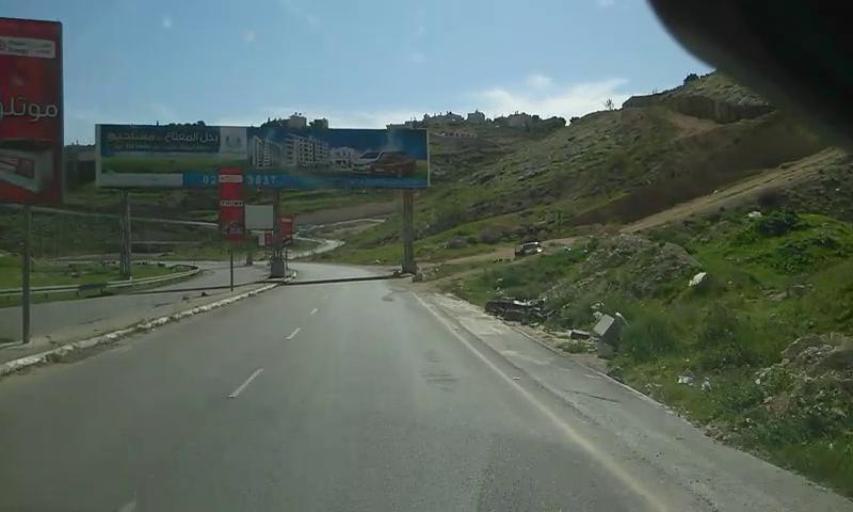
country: PS
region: West Bank
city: Al `Ayzariyah
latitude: 31.7477
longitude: 35.2871
